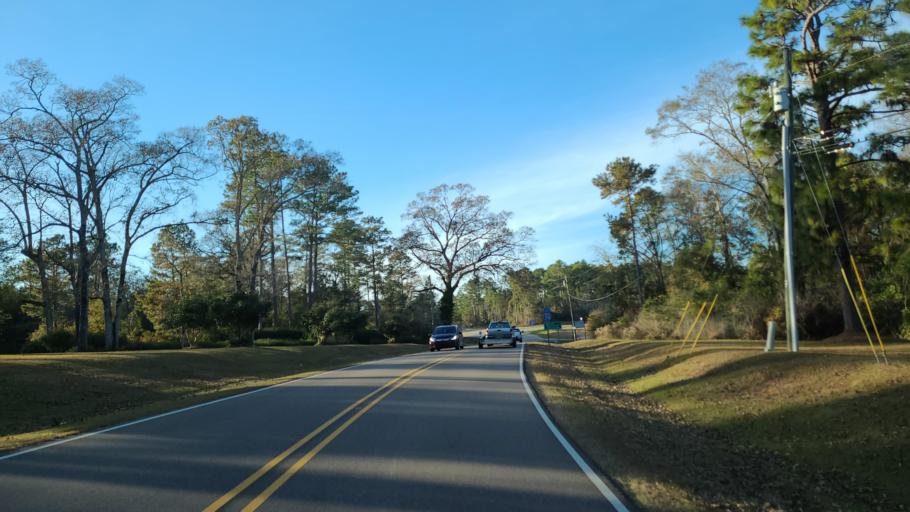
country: US
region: Mississippi
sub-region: Lamar County
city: Purvis
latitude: 31.1381
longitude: -89.3651
